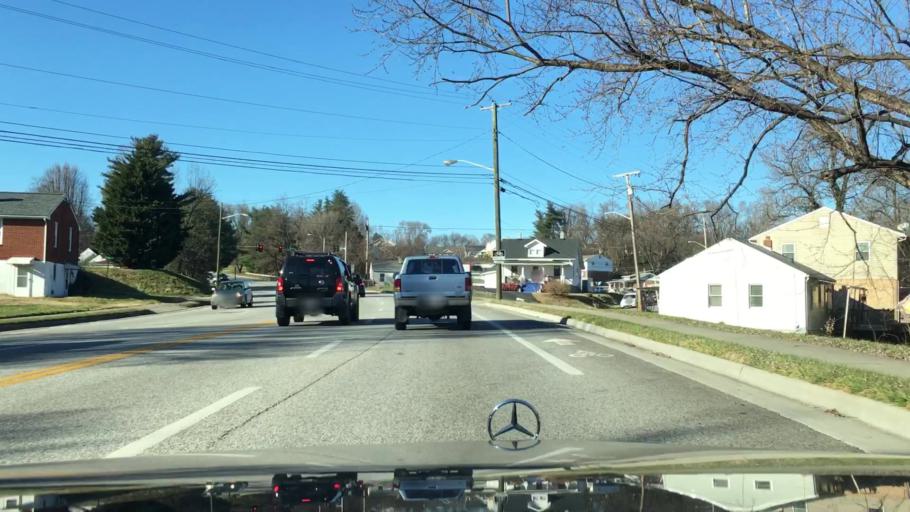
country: US
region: Virginia
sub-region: Roanoke County
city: Vinton
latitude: 37.2852
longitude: -79.9009
